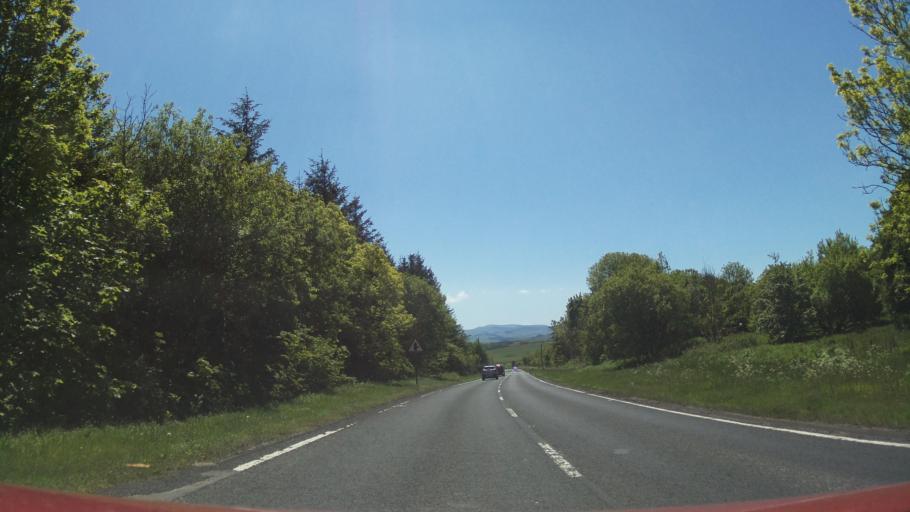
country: GB
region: Scotland
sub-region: The Scottish Borders
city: Hawick
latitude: 55.4592
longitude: -2.7793
